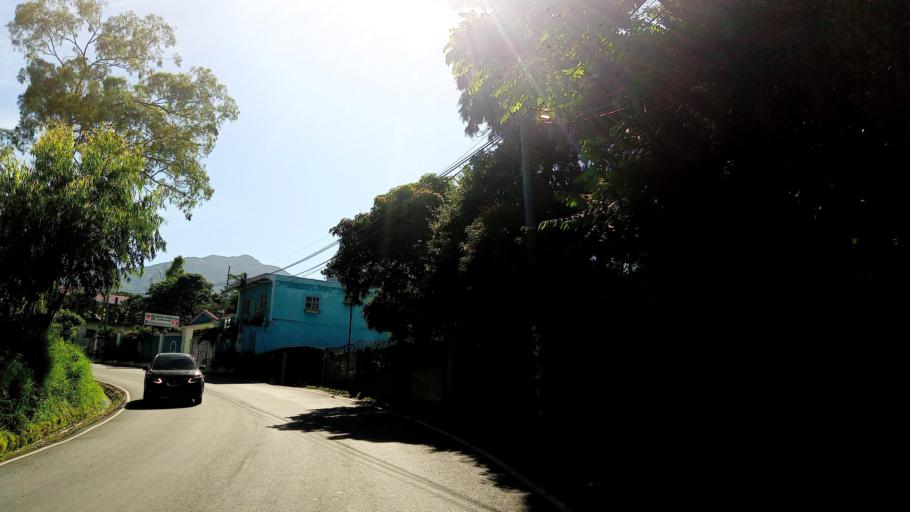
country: HN
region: Ocotepeque
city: Antigua Ocotepeque
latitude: 14.3136
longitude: -89.1671
